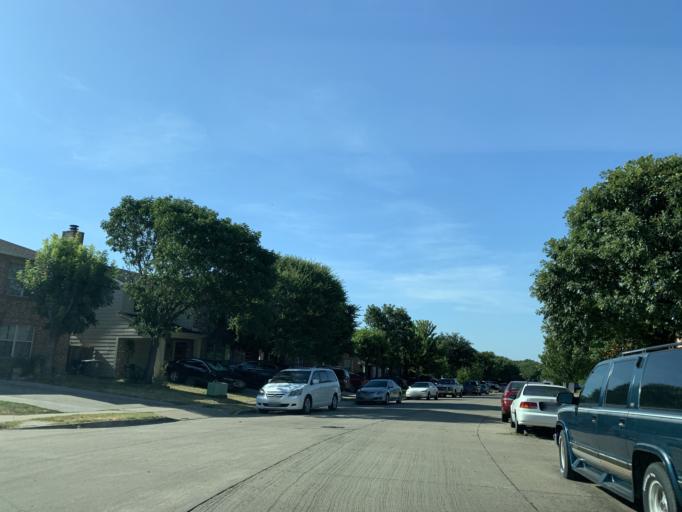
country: US
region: Texas
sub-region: Dallas County
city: Cockrell Hill
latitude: 32.7066
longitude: -96.8961
